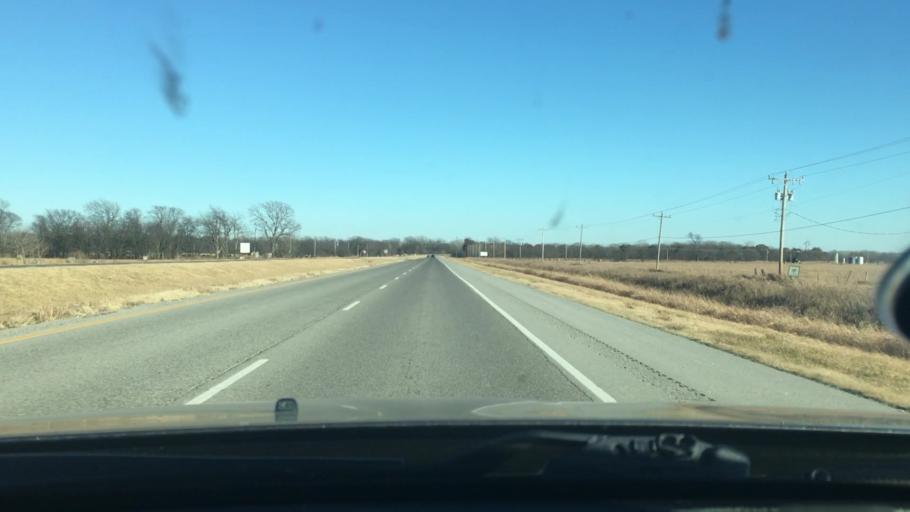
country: US
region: Oklahoma
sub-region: Murray County
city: Davis
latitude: 34.5064
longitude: -97.1629
